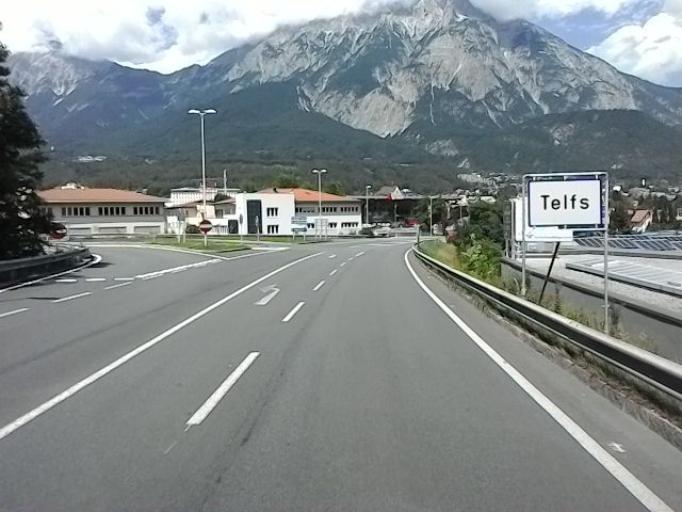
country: AT
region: Tyrol
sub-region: Politischer Bezirk Innsbruck Land
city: Telfs
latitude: 47.3022
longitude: 11.0704
